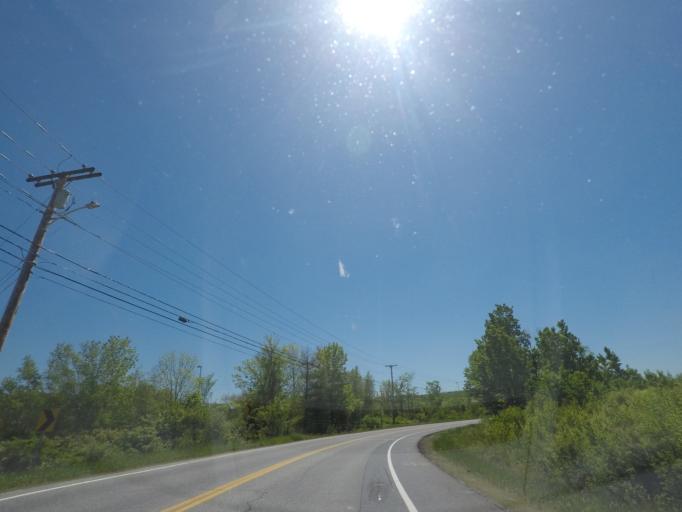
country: US
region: Maine
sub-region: Kennebec County
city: Augusta
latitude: 44.3105
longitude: -69.8100
